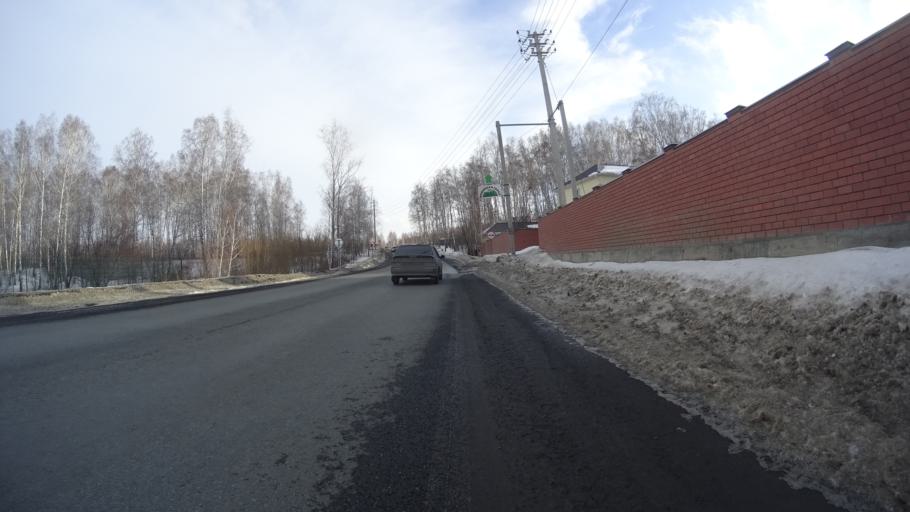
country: RU
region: Chelyabinsk
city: Sargazy
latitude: 55.1295
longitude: 61.2880
